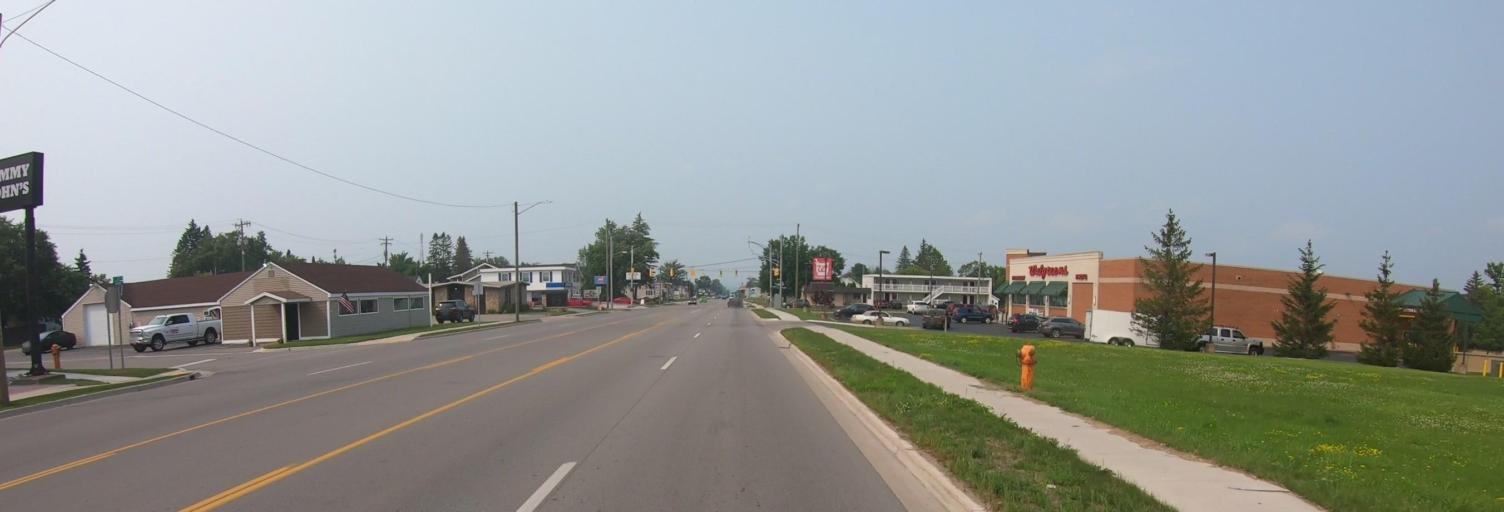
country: US
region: Michigan
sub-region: Chippewa County
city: Sault Ste. Marie
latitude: 46.4797
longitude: -84.3537
